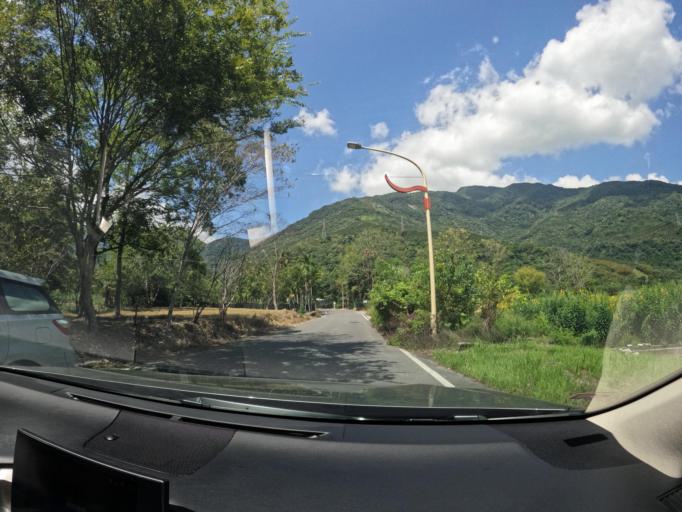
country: TW
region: Taiwan
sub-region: Hualien
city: Hualian
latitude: 23.7181
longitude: 121.4074
